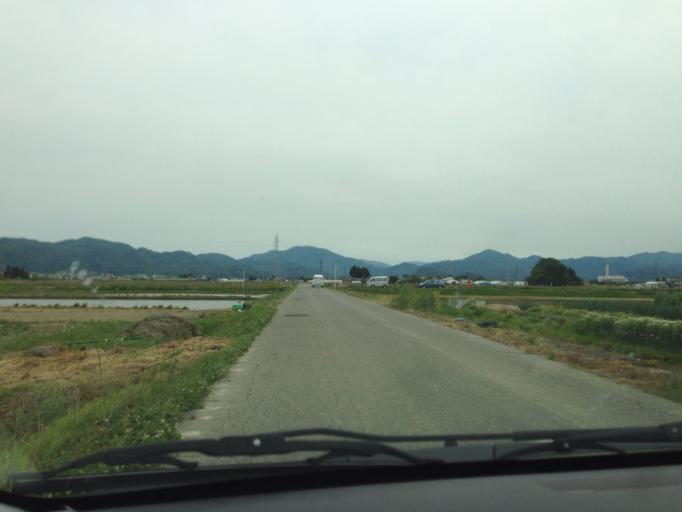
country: JP
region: Fukushima
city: Kitakata
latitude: 37.5115
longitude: 139.8984
